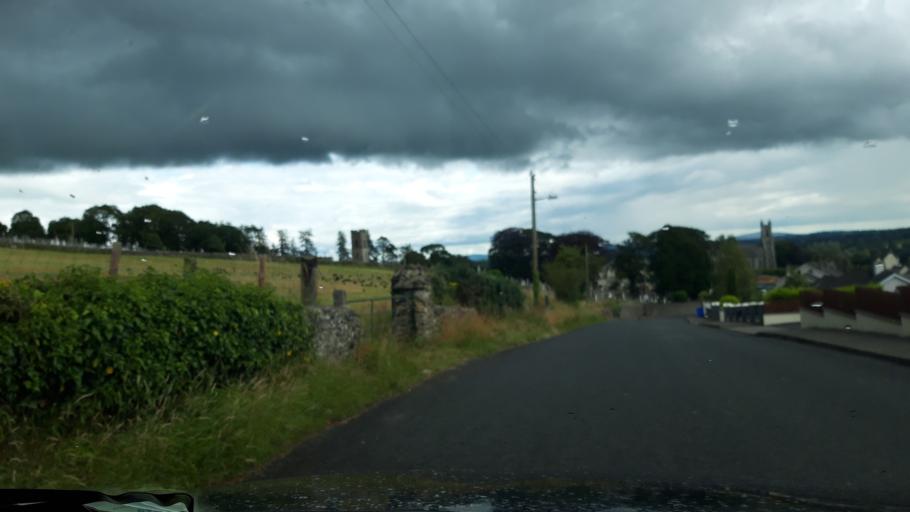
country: IE
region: Leinster
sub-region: Wicklow
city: Baltinglass
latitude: 52.9436
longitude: -6.7059
